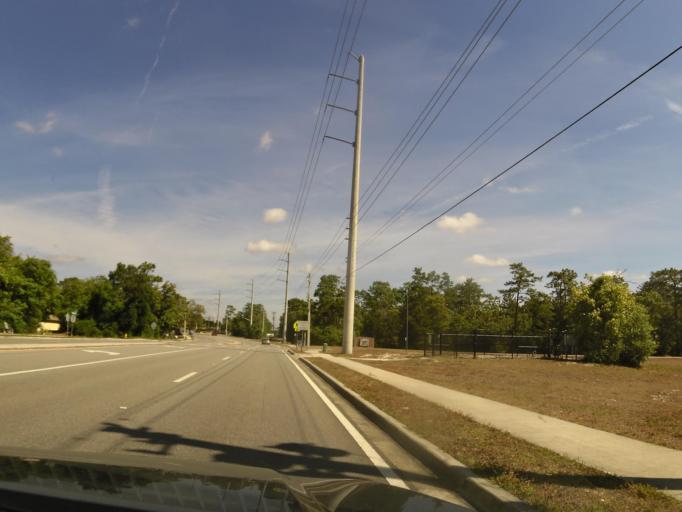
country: US
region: Florida
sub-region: Volusia County
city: Deltona
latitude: 28.8950
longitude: -81.1656
